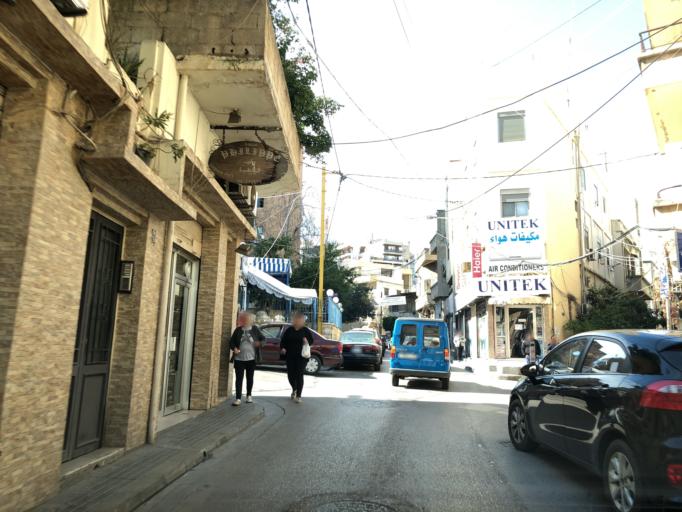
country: LB
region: Beyrouth
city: Beirut
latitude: 33.8883
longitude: 35.5285
